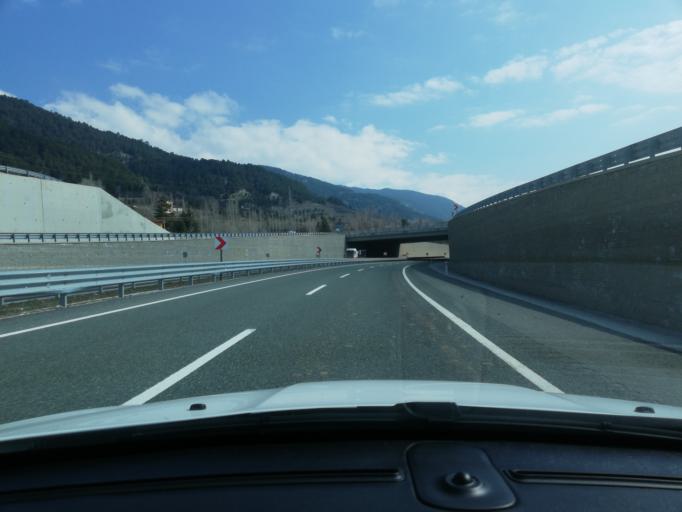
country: TR
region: Cankiri
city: Ilgaz
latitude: 41.0255
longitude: 33.7181
